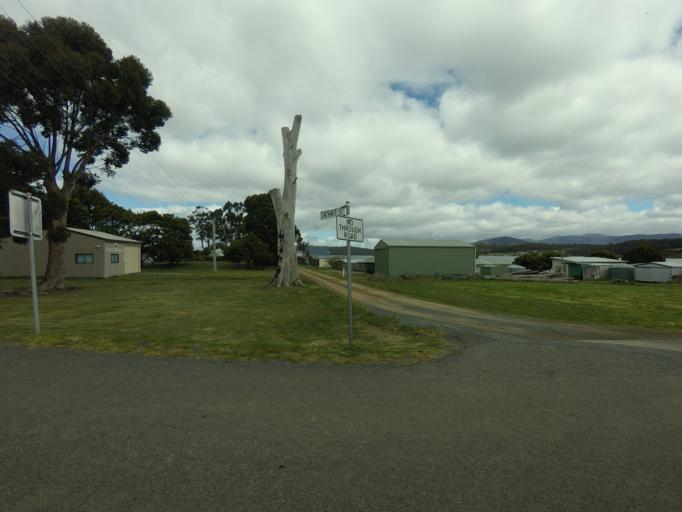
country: AU
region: Tasmania
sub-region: Huon Valley
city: Geeveston
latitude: -43.4338
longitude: 146.9796
